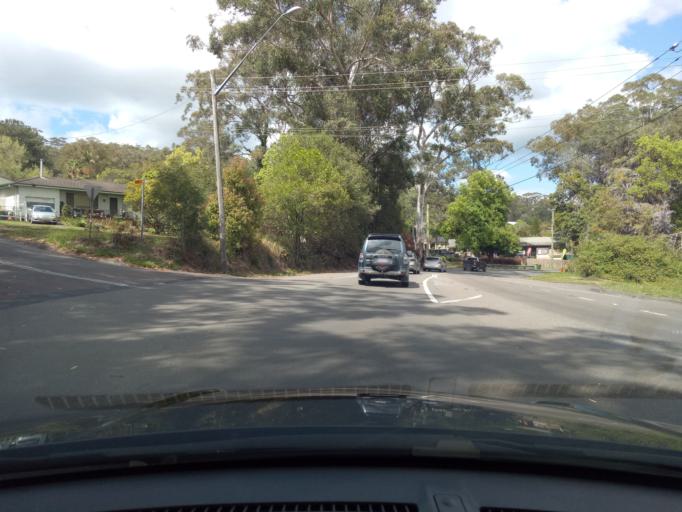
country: AU
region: New South Wales
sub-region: Gosford Shire
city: Narara
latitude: -33.3887
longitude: 151.3552
